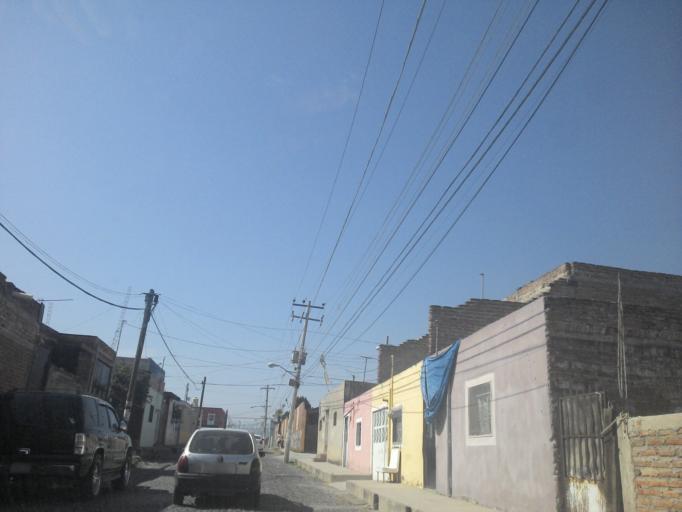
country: MX
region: Jalisco
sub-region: San Pedro Tlaquepaque
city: Paseo del Prado
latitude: 20.5886
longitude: -103.3864
